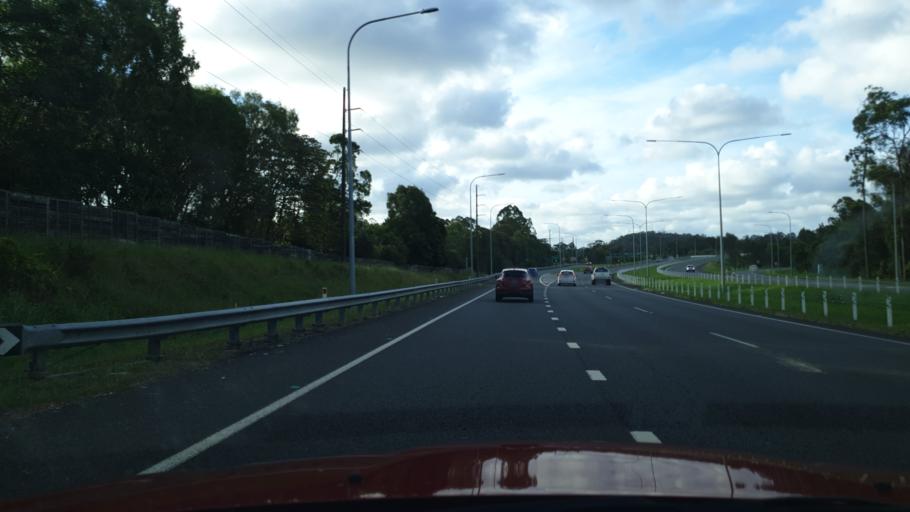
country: AU
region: Queensland
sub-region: Sunshine Coast
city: Buderim
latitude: -26.6650
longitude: 153.0687
